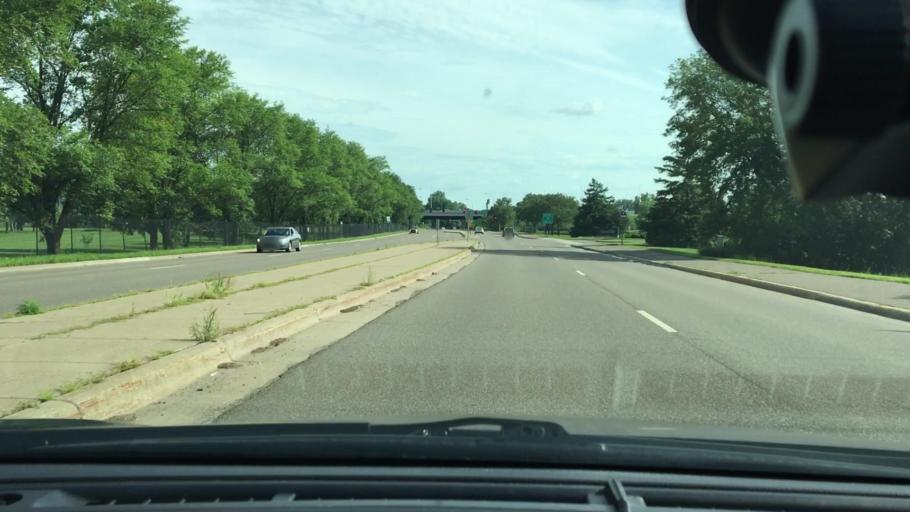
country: US
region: Minnesota
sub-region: Hennepin County
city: Saint Louis Park
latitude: 44.9779
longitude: -93.3906
